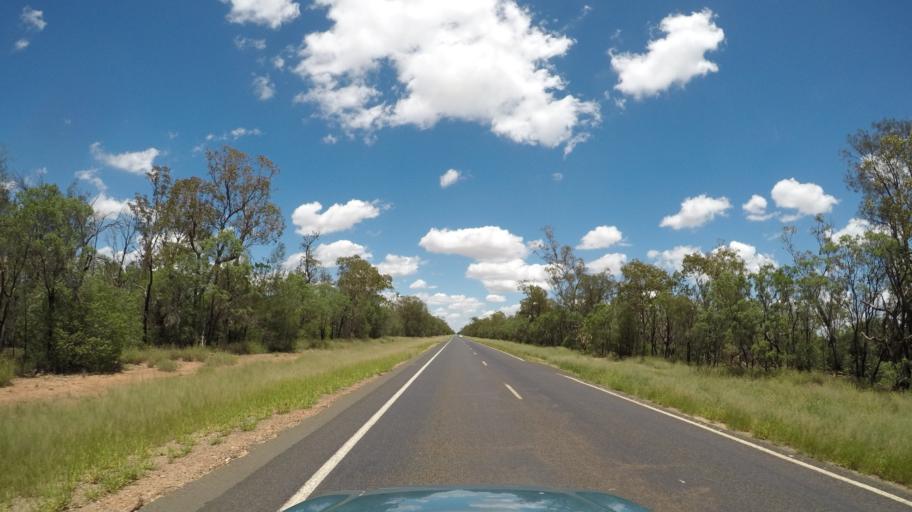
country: AU
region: Queensland
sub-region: Goondiwindi
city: Goondiwindi
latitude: -28.1603
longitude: 150.6309
